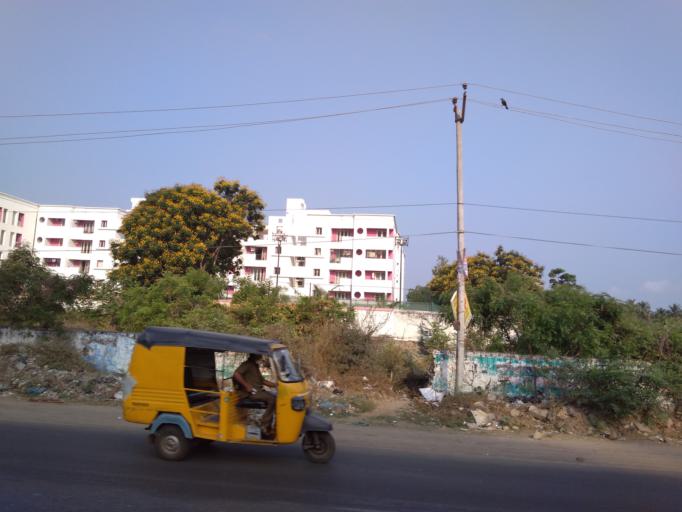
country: IN
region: Tamil Nadu
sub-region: Kancheepuram
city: Vengavasal
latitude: 12.8121
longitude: 80.2287
